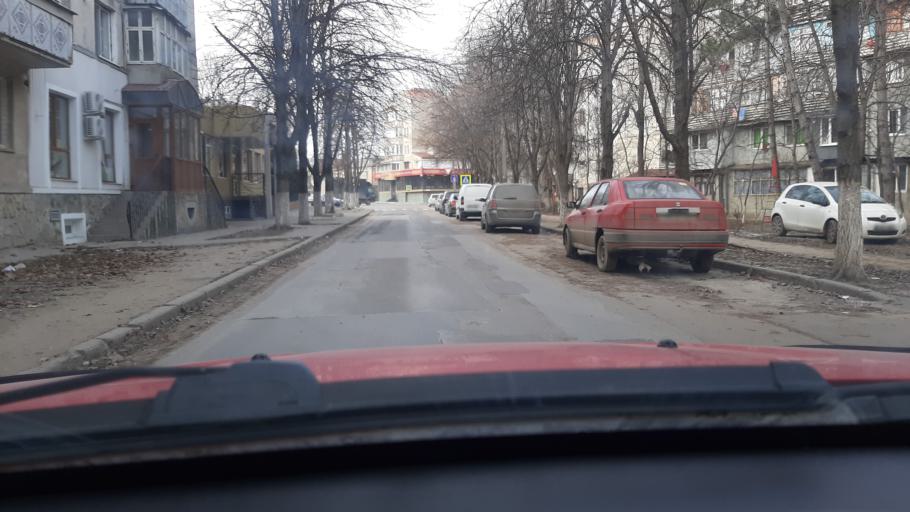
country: MD
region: Chisinau
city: Chisinau
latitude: 47.0317
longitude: 28.7926
